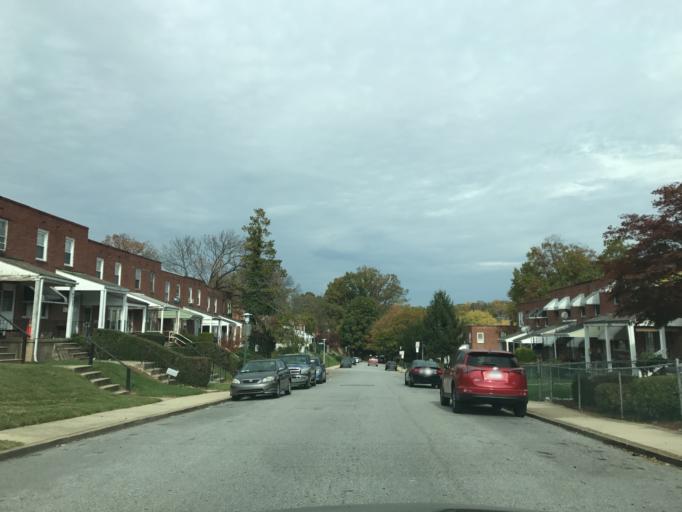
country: US
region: Maryland
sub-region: Baltimore County
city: Lochearn
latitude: 39.3424
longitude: -76.6612
